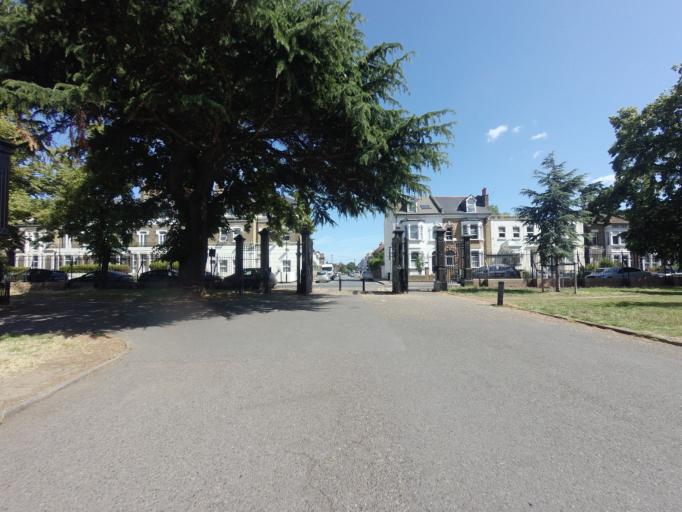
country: GB
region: England
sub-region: Greater London
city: East Ham
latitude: 51.5412
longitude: 0.0200
